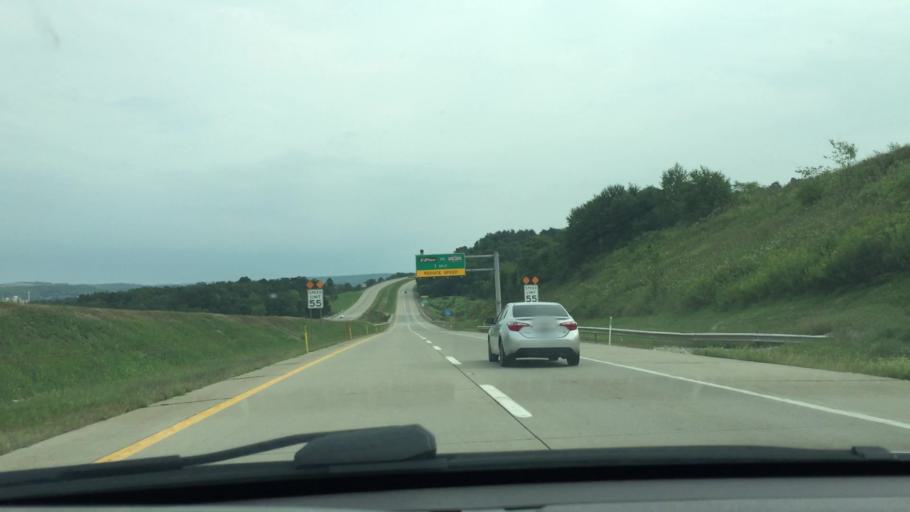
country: US
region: Pennsylvania
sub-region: Lawrence County
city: Oakland
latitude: 40.9598
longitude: -80.3970
